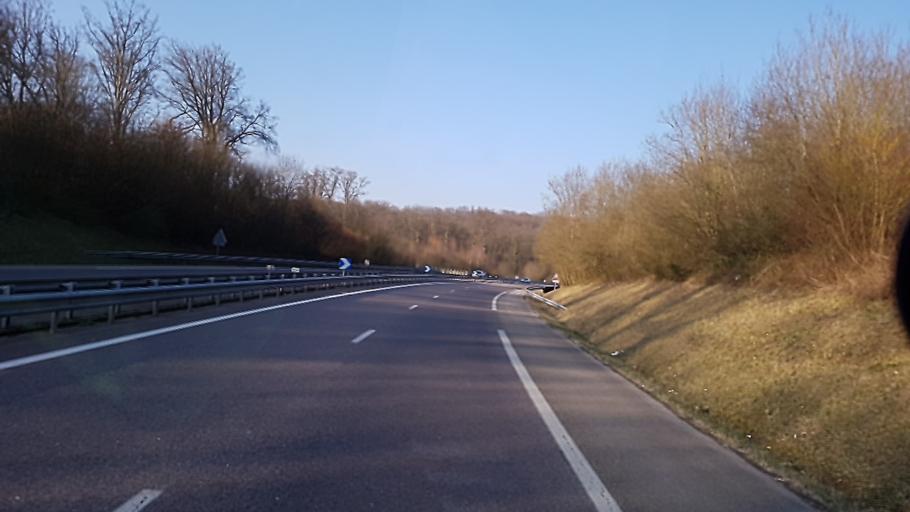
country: DE
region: Saarland
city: Kleinblittersdorf
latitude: 49.1274
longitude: 7.0344
